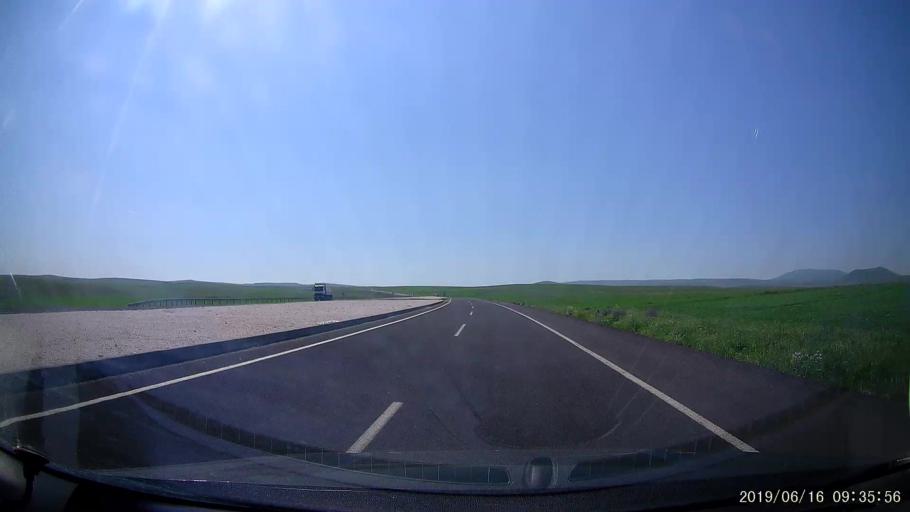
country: TR
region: Kars
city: Kars
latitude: 40.5640
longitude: 43.1641
